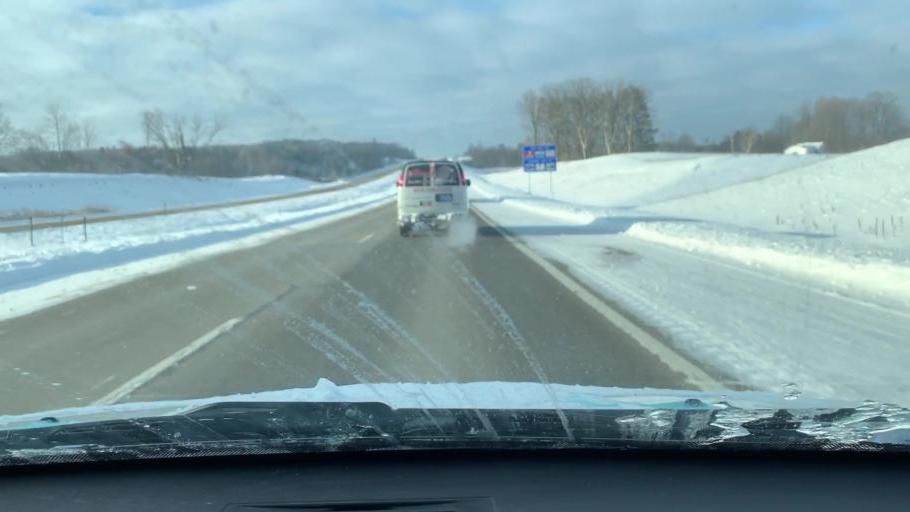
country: US
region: Michigan
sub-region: Wexford County
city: Cadillac
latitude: 44.2316
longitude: -85.3794
